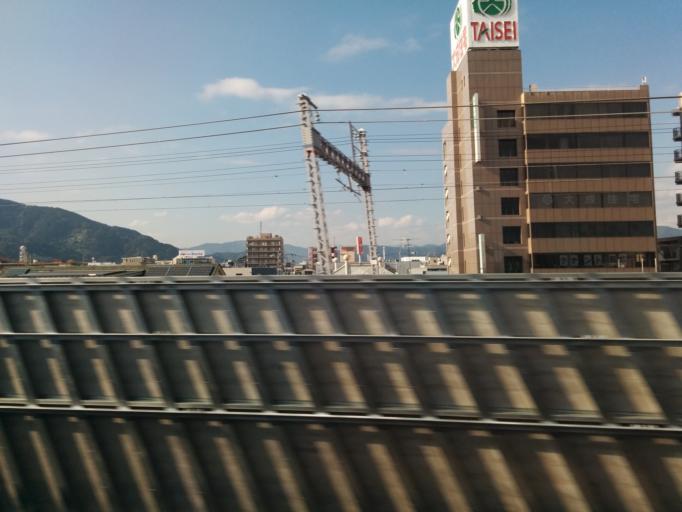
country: JP
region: Shizuoka
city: Shizuoka-shi
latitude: 34.9625
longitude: 138.3772
